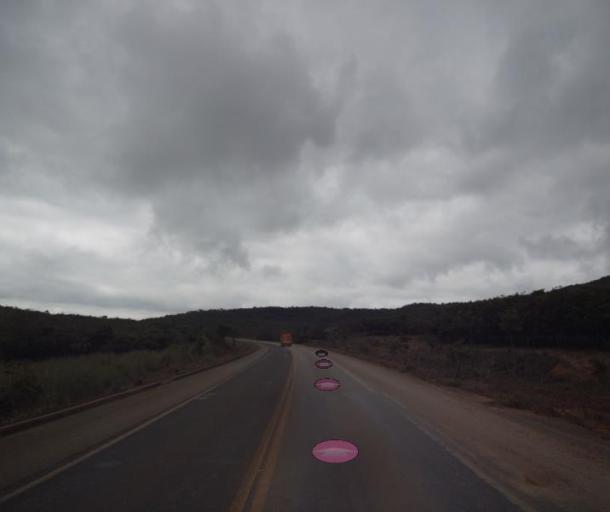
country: BR
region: Goias
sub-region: Barro Alto
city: Barro Alto
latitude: -14.9322
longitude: -48.9489
